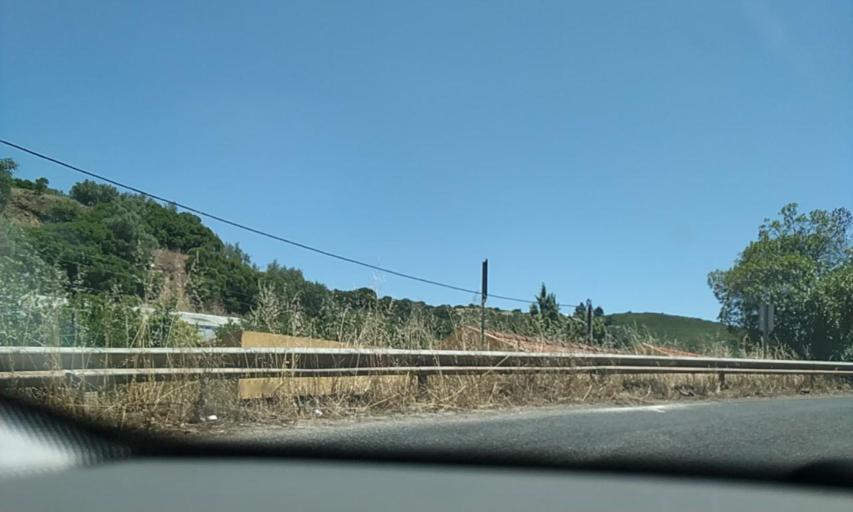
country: PT
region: Lisbon
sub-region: Odivelas
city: Canecas
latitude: 38.8642
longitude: -9.2106
